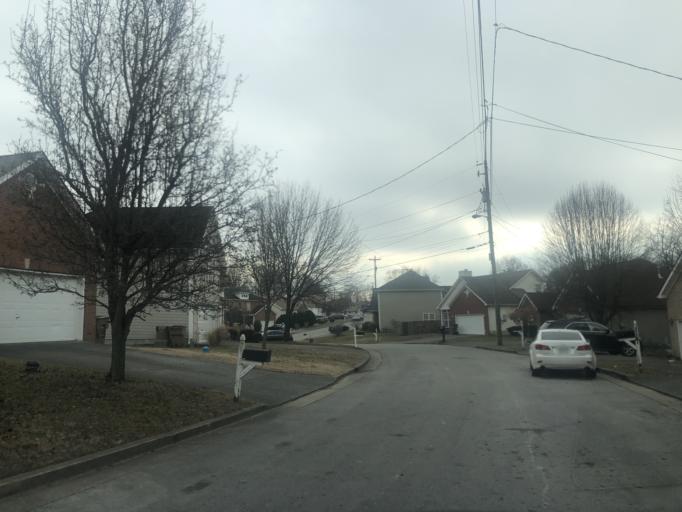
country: US
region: Tennessee
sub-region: Rutherford County
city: La Vergne
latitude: 36.0829
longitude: -86.6453
